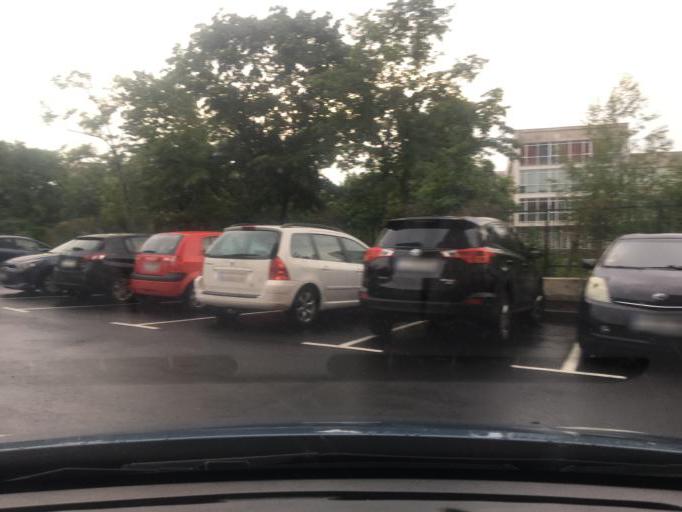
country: BG
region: Burgas
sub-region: Obshtina Burgas
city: Burgas
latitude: 42.5138
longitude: 27.4708
